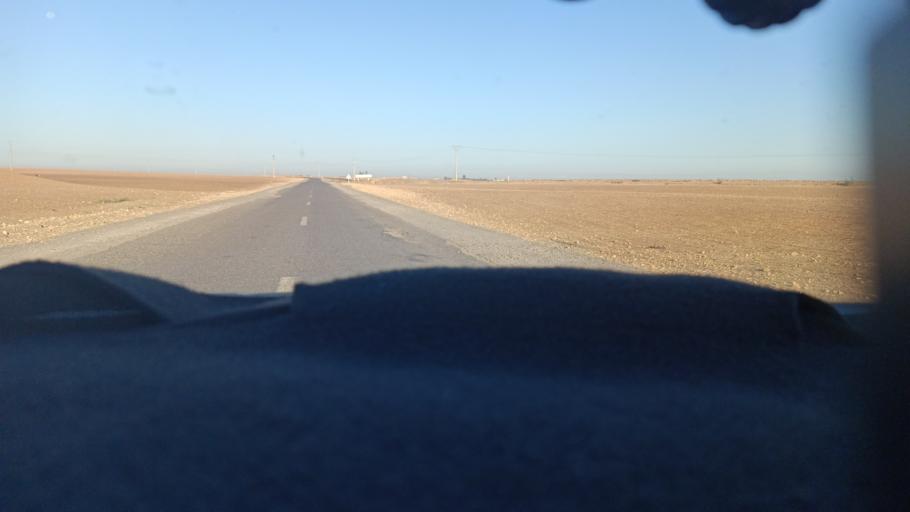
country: MA
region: Doukkala-Abda
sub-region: Safi
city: Youssoufia
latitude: 32.3699
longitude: -8.6280
